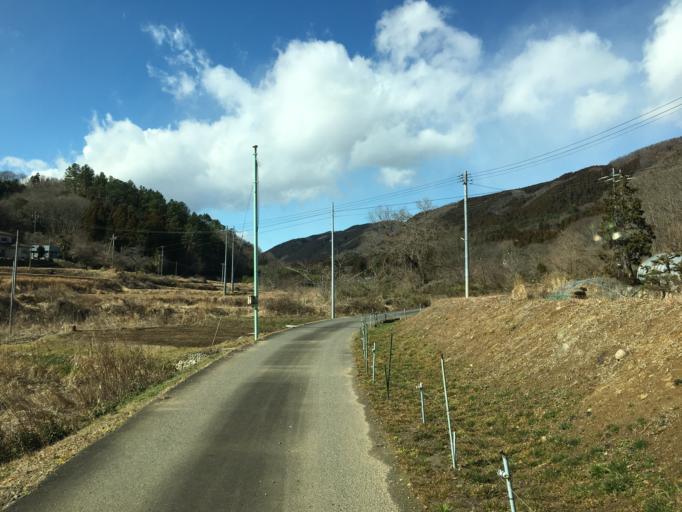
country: JP
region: Fukushima
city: Iwaki
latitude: 37.0063
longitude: 140.7958
